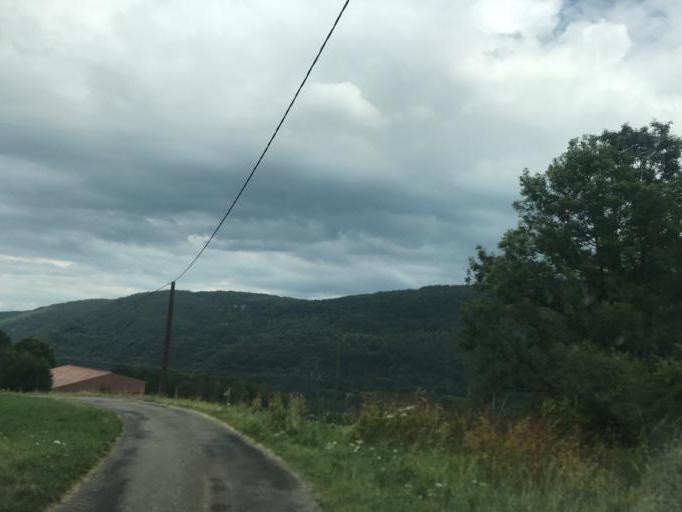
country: FR
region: Franche-Comte
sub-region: Departement du Jura
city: Longchaumois
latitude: 46.4684
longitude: 5.8891
